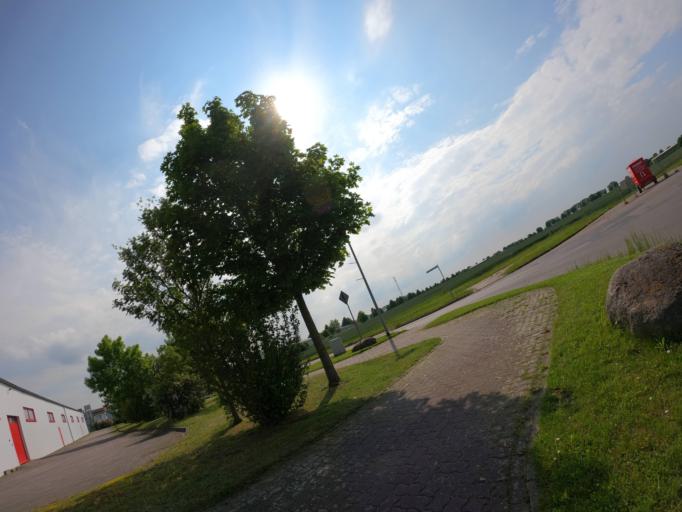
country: DE
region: Mecklenburg-Vorpommern
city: Wendorf
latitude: 54.2827
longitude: 13.0577
